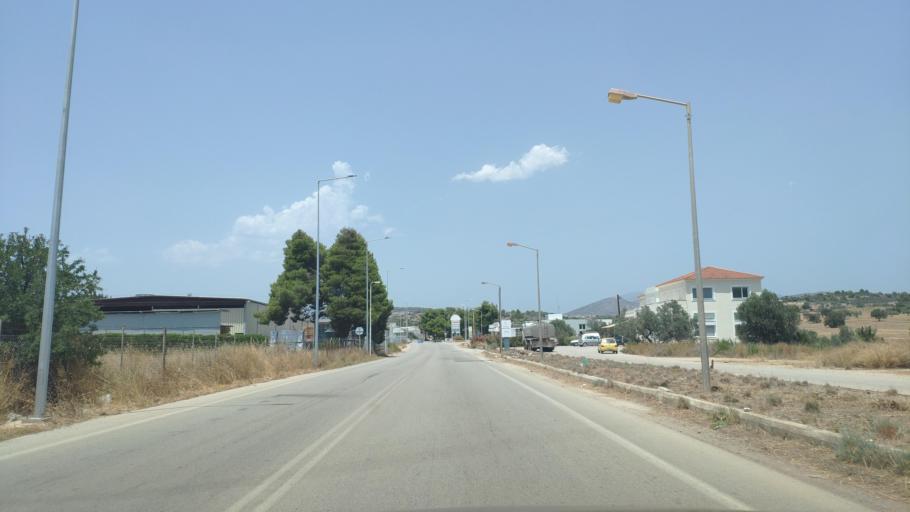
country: GR
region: Peloponnese
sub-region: Nomos Argolidos
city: Porto Cheli
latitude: 37.3465
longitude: 23.1575
